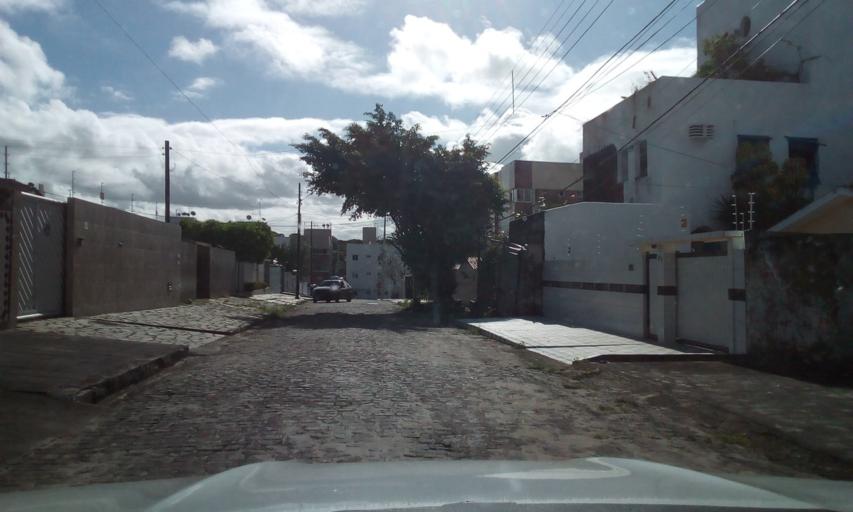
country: BR
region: Paraiba
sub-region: Joao Pessoa
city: Joao Pessoa
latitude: -7.1432
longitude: -34.8424
